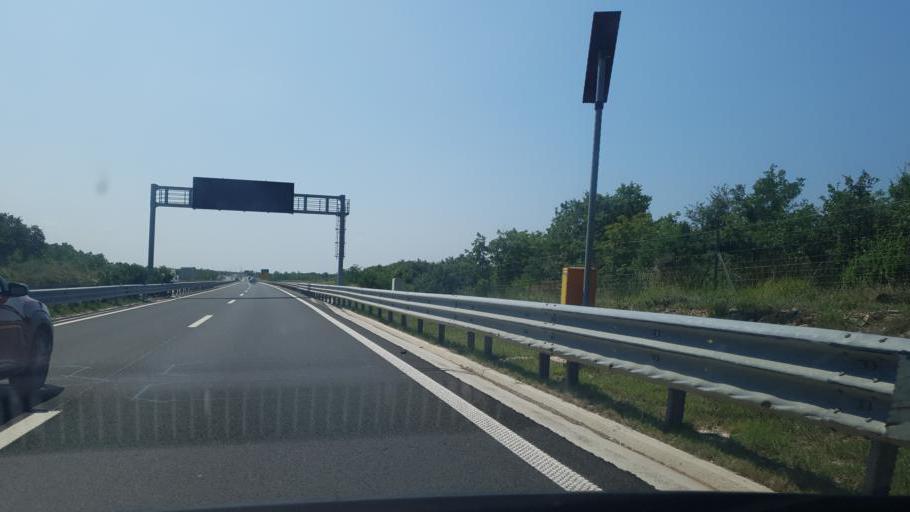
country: HR
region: Istarska
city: Vodnjan
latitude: 44.9957
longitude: 13.8400
